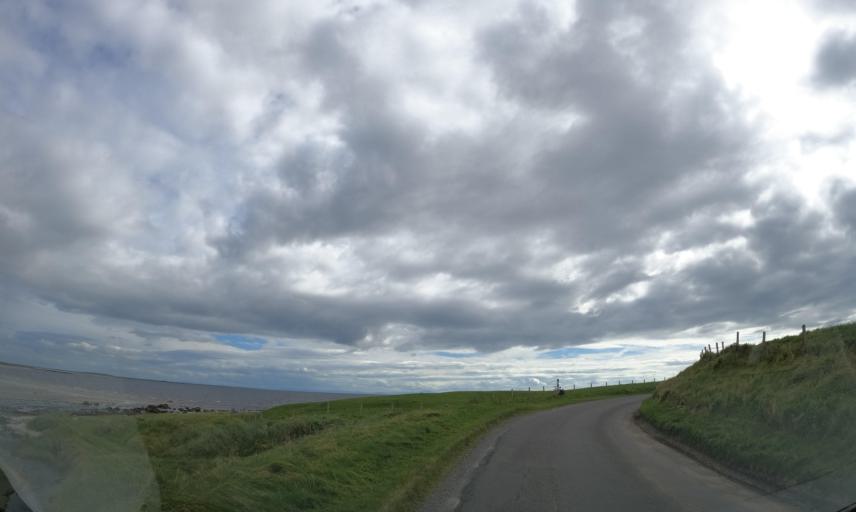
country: GB
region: Scotland
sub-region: Eilean Siar
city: Barra
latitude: 56.4701
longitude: -6.8980
